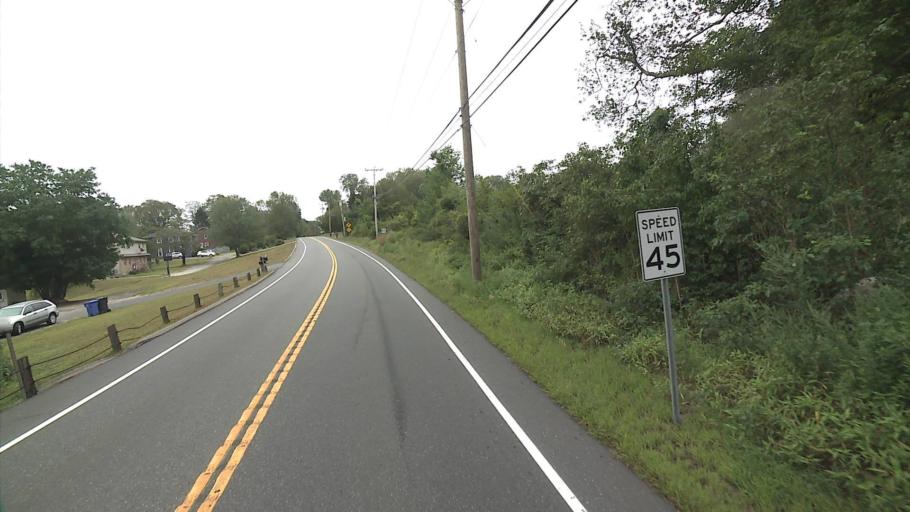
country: US
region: Connecticut
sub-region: New London County
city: Colchester
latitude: 41.5101
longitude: -72.2905
